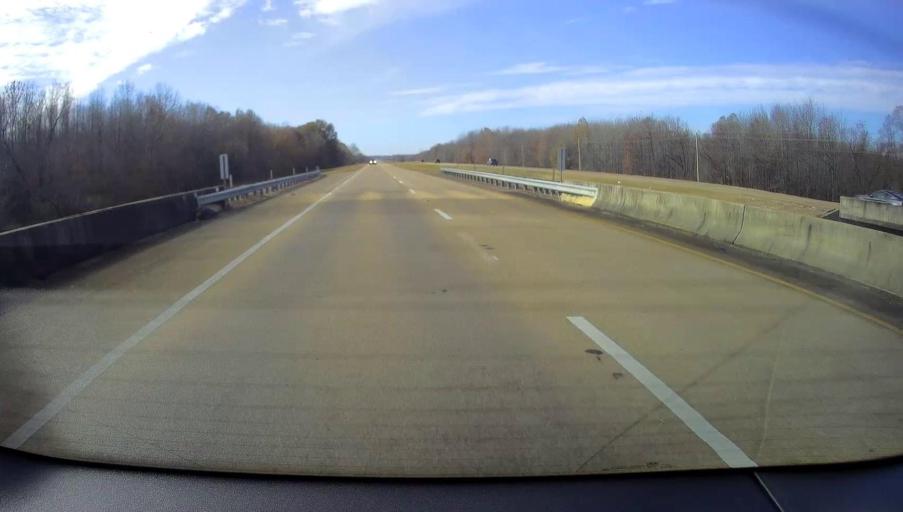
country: US
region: Mississippi
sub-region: Alcorn County
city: Corinth
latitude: 34.9310
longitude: -88.5906
